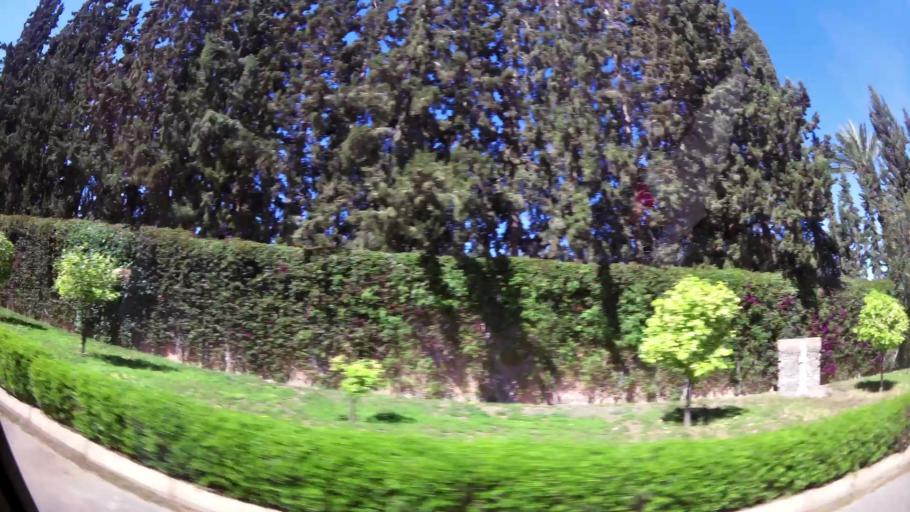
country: MA
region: Marrakech-Tensift-Al Haouz
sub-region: Marrakech
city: Marrakesh
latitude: 31.6555
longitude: -7.9632
